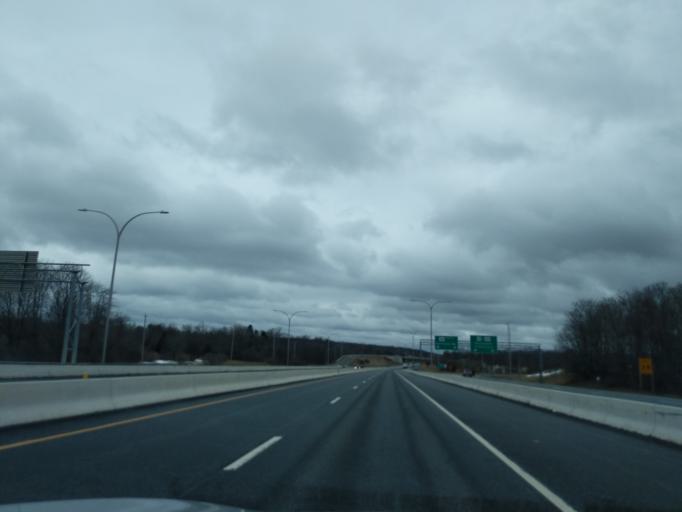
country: US
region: Rhode Island
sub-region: Providence County
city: Cumberland Hill
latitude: 41.9463
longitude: -71.4801
